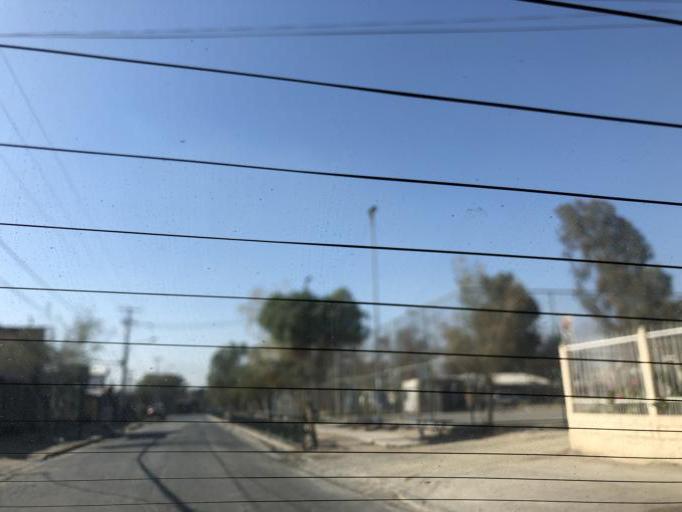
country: CL
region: Santiago Metropolitan
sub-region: Provincia de Cordillera
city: Puente Alto
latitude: -33.6132
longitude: -70.5886
